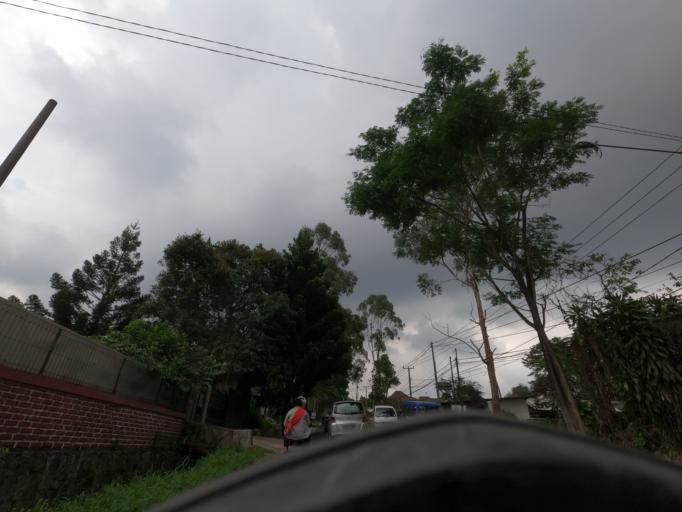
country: ID
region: West Java
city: Sukabumi
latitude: -6.7599
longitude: 107.0492
